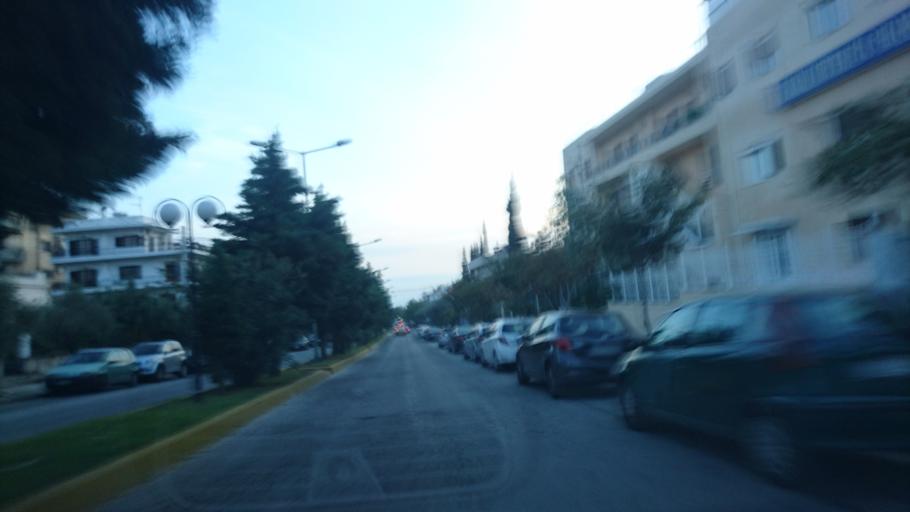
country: GR
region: Attica
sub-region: Nomarchia Athinas
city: Ilioupoli
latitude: 37.9350
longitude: 23.7579
